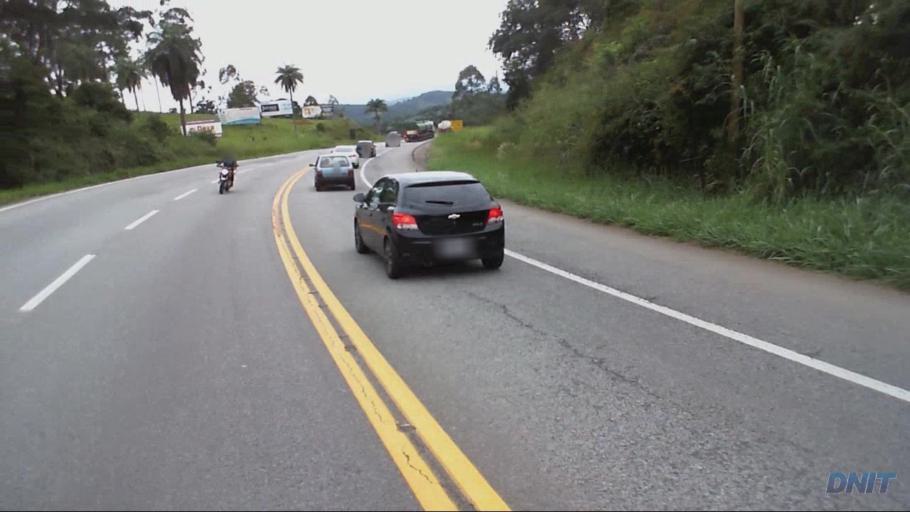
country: BR
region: Minas Gerais
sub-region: Caete
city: Caete
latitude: -19.7406
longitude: -43.5177
